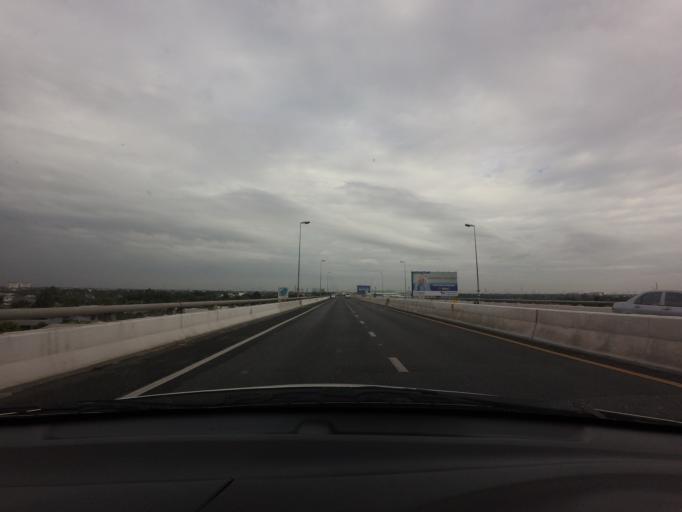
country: TH
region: Bangkok
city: Taling Chan
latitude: 13.7826
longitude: 100.4136
